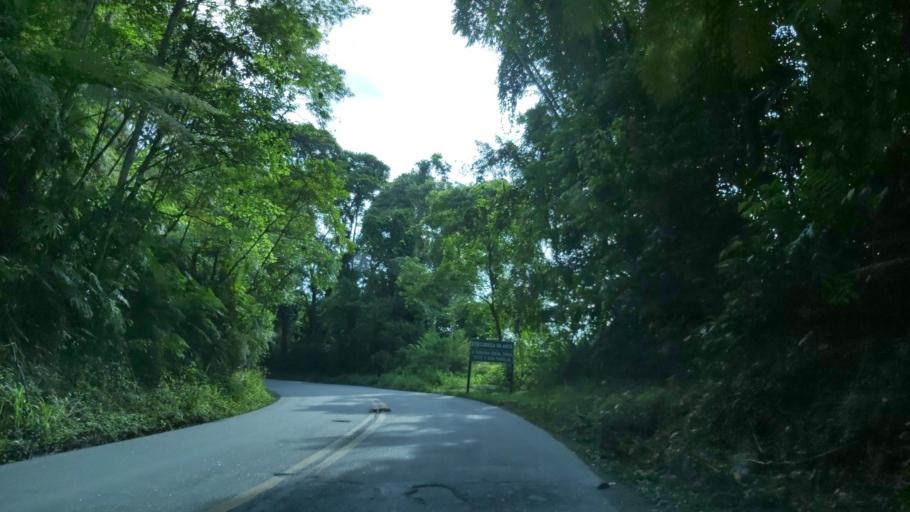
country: BR
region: Sao Paulo
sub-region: Juquia
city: Juquia
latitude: -24.0889
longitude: -47.6155
